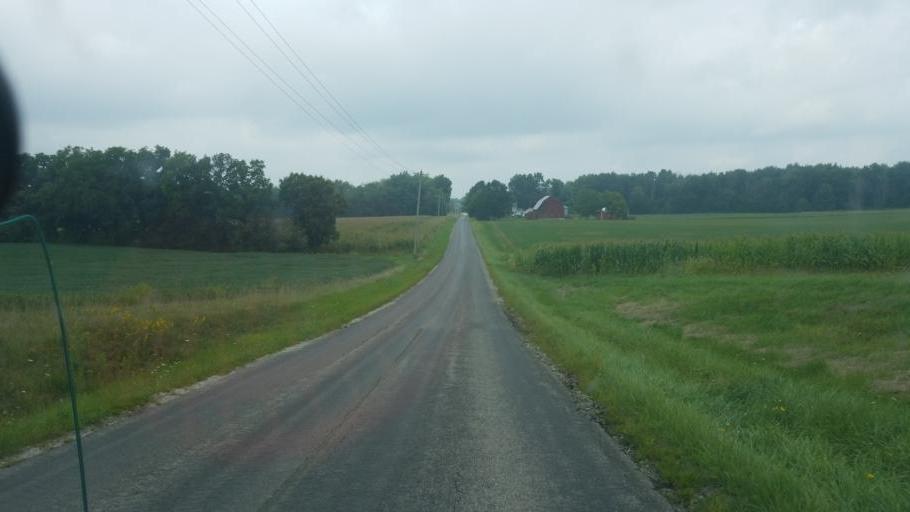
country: US
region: Ohio
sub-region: Huron County
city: Greenwich
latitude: 40.9786
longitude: -82.4722
